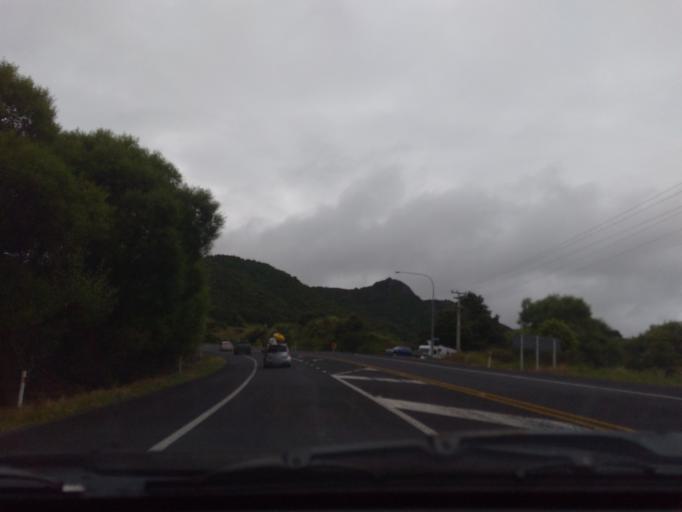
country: NZ
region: Auckland
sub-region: Auckland
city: Wellsford
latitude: -36.1233
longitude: 174.4349
